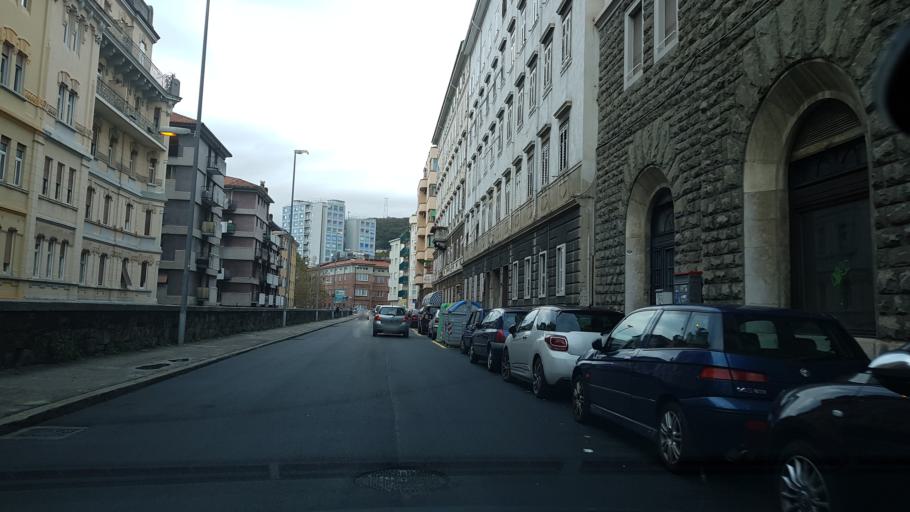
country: IT
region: Friuli Venezia Giulia
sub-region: Provincia di Trieste
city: Trieste
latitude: 45.6626
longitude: 13.7712
